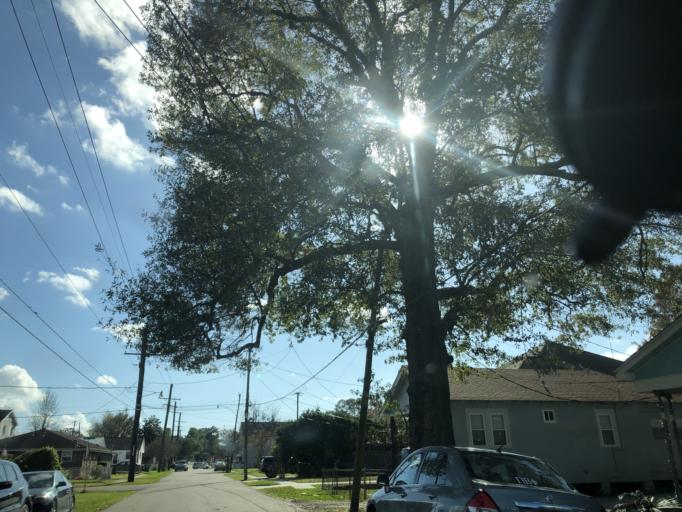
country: US
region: Louisiana
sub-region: Jefferson Parish
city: Metairie Terrace
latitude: 29.9835
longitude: -90.1615
